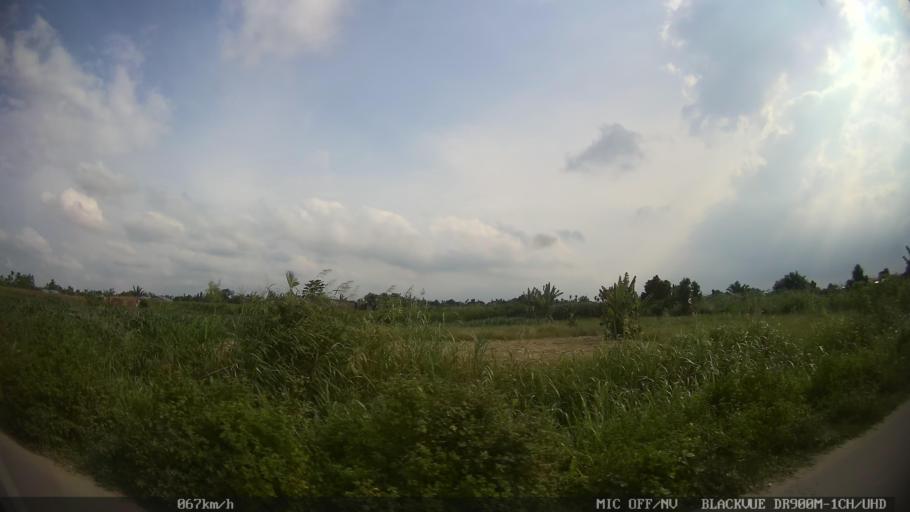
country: ID
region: North Sumatra
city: Medan
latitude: 3.5730
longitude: 98.7688
